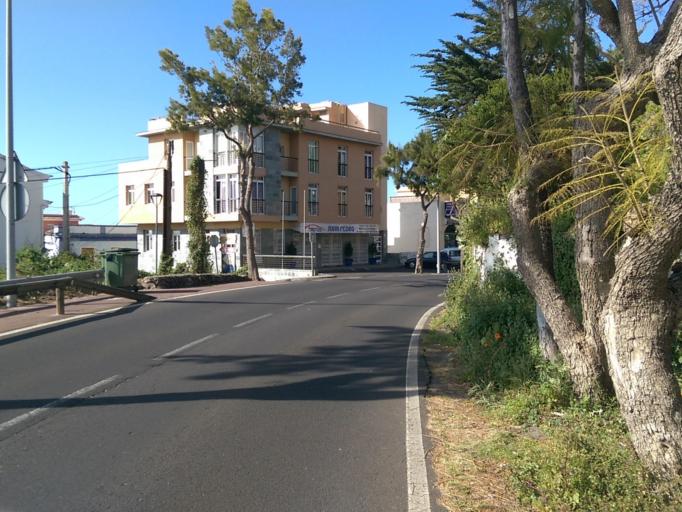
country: ES
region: Canary Islands
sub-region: Provincia de Santa Cruz de Tenerife
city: La Matanza de Acentejo
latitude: 28.4456
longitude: -16.4589
